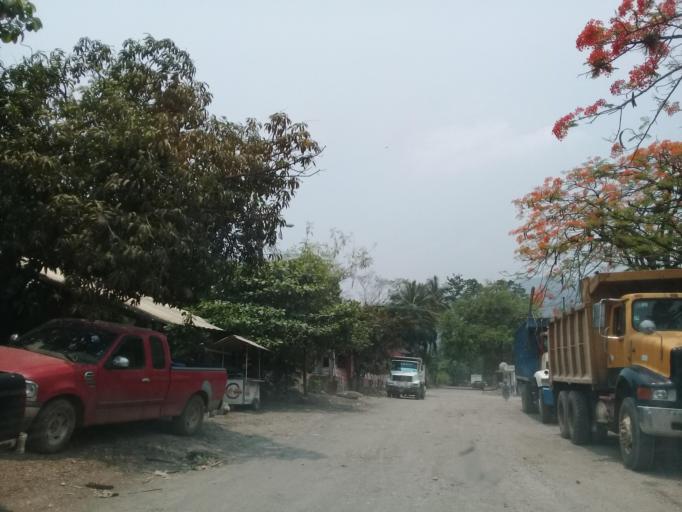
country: MX
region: Veracruz
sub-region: Tezonapa
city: Laguna Chica (Pueblo Nuevo)
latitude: 18.5432
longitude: -96.7351
